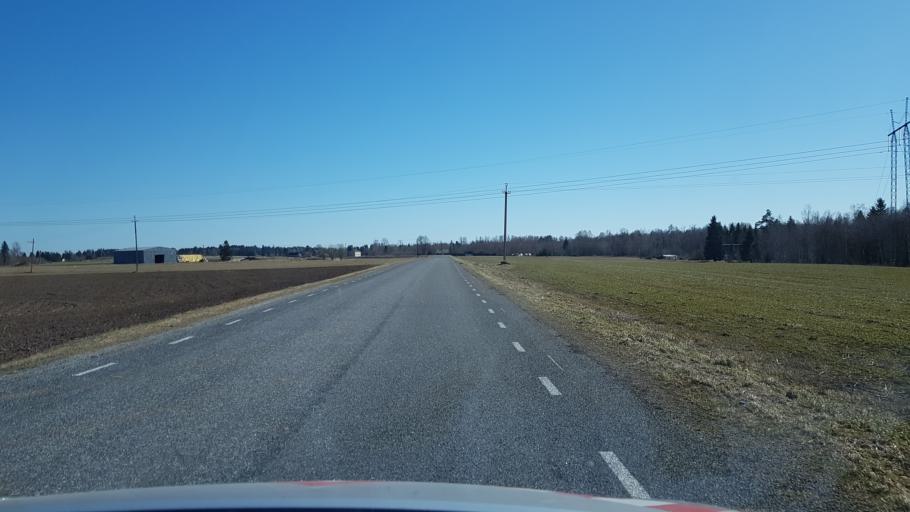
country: EE
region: Laeaene-Virumaa
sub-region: Someru vald
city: Someru
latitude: 59.3764
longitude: 26.4424
